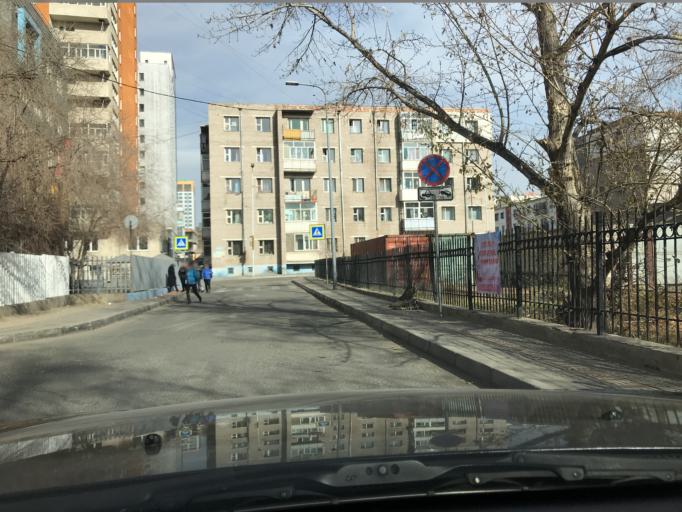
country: MN
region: Ulaanbaatar
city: Ulaanbaatar
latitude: 47.9176
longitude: 106.9030
